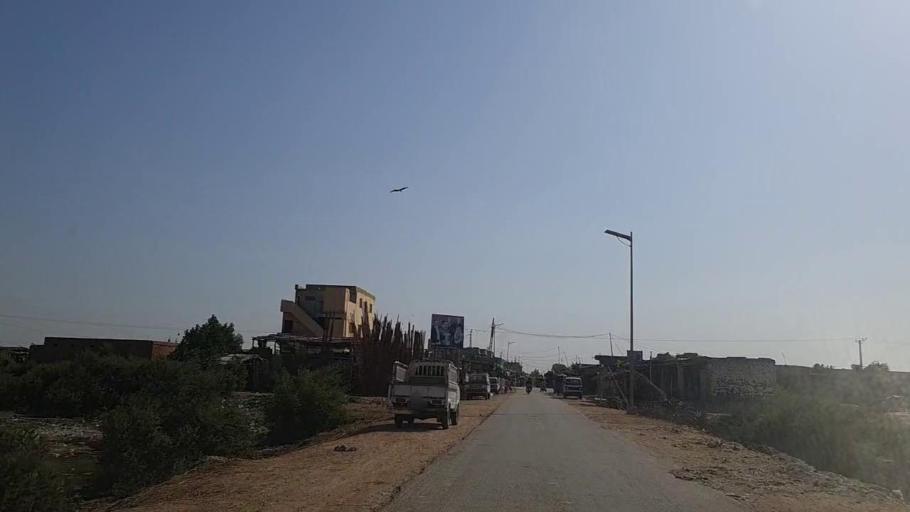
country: PK
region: Sindh
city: Mirpur Batoro
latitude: 24.6191
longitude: 68.2952
